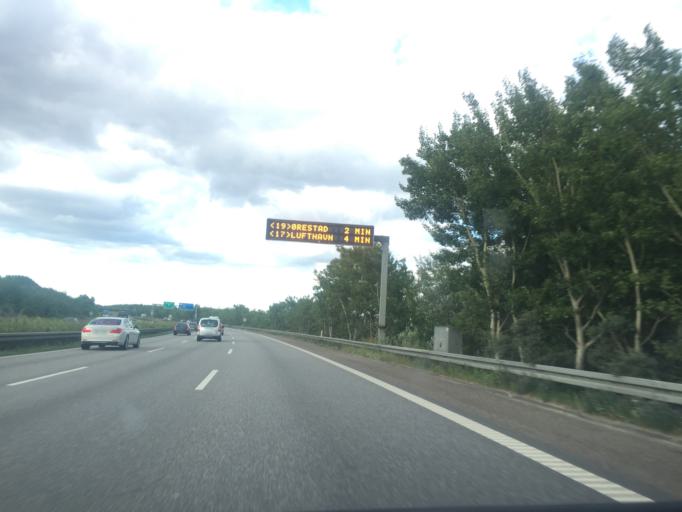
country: DK
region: Capital Region
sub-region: Frederiksberg Kommune
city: Frederiksberg
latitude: 55.6164
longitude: 12.5249
